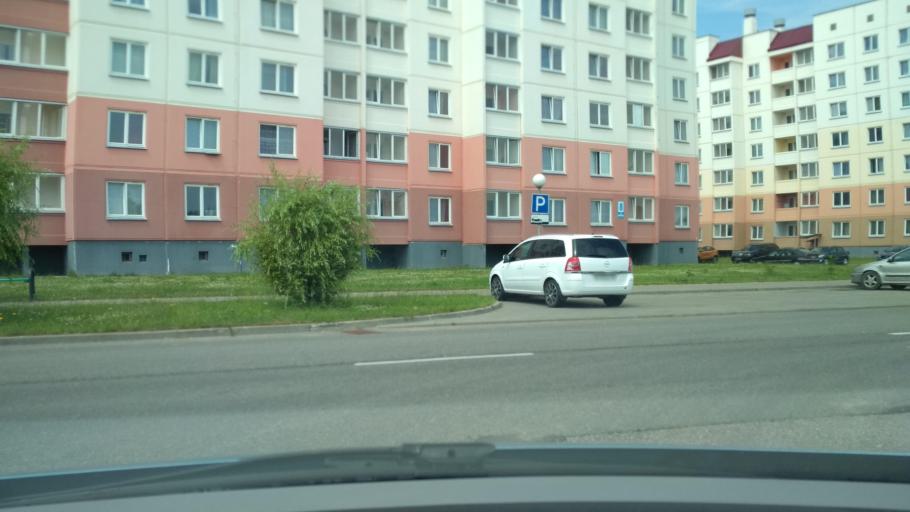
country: BY
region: Grodnenskaya
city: Astravyets
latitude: 54.6070
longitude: 25.9739
